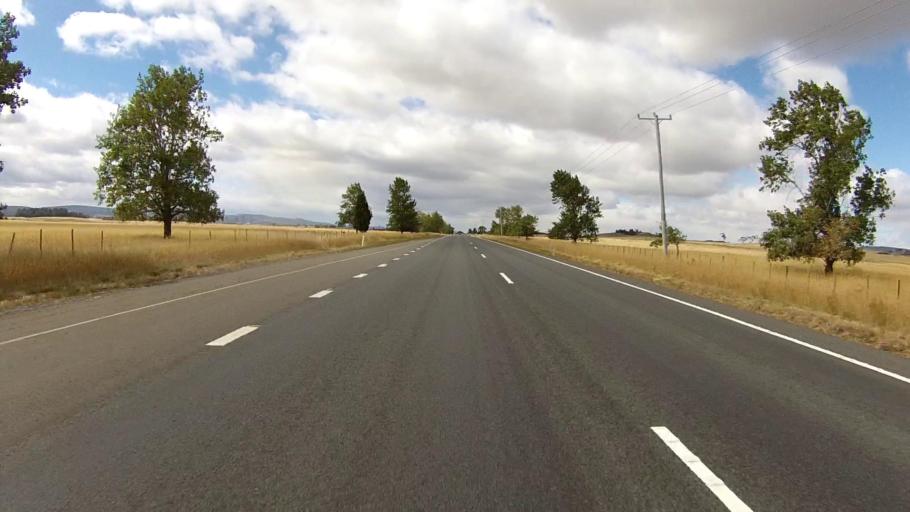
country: AU
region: Tasmania
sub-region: Northern Midlands
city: Evandale
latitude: -41.8874
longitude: 147.4686
